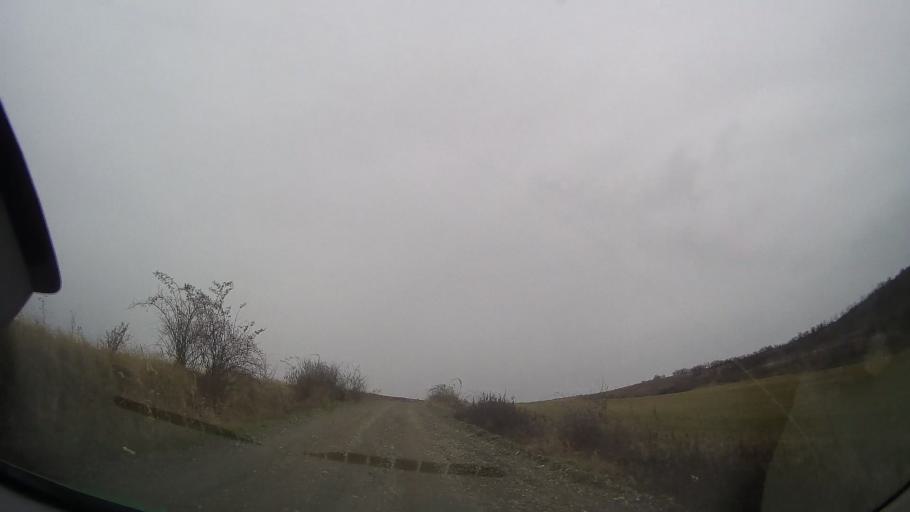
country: RO
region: Mures
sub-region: Comuna Ceausu de Campie
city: Ceausu de Campie
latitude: 46.6566
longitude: 24.4895
